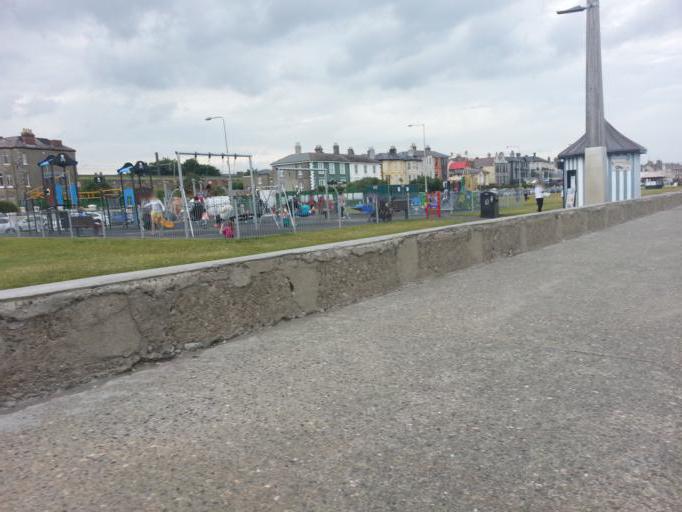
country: IE
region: Leinster
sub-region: Wicklow
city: Bray
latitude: 53.2004
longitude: -6.0960
